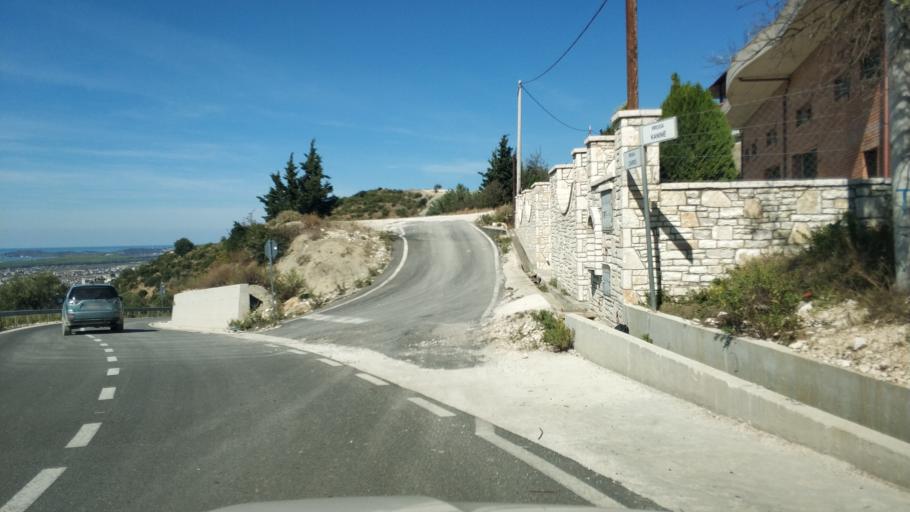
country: AL
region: Vlore
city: Vlore
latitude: 40.4555
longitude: 19.5147
